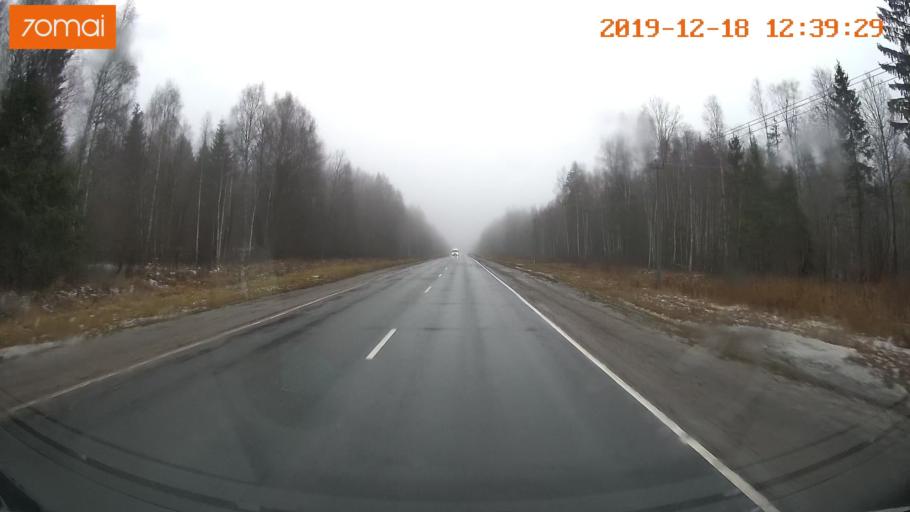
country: RU
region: Moskovskaya
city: Vysokovsk
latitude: 56.1655
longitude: 36.6117
